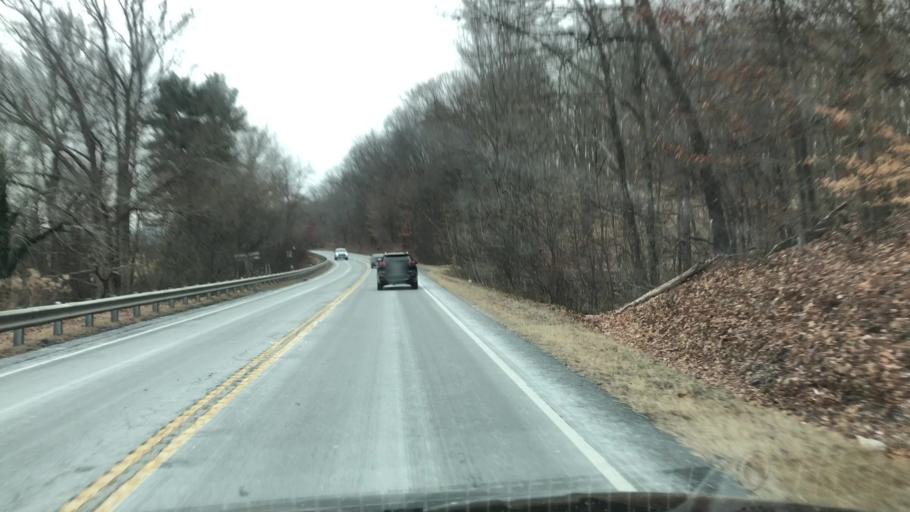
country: US
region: Virginia
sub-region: Loudoun County
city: Leesburg
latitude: 39.0456
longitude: -77.6218
